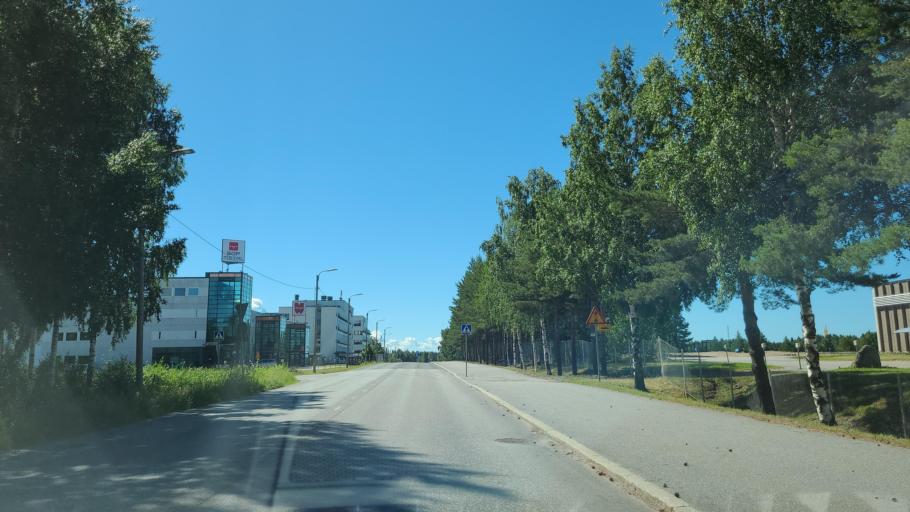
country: FI
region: Ostrobothnia
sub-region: Vaasa
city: Ristinummi
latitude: 63.0592
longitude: 21.7330
